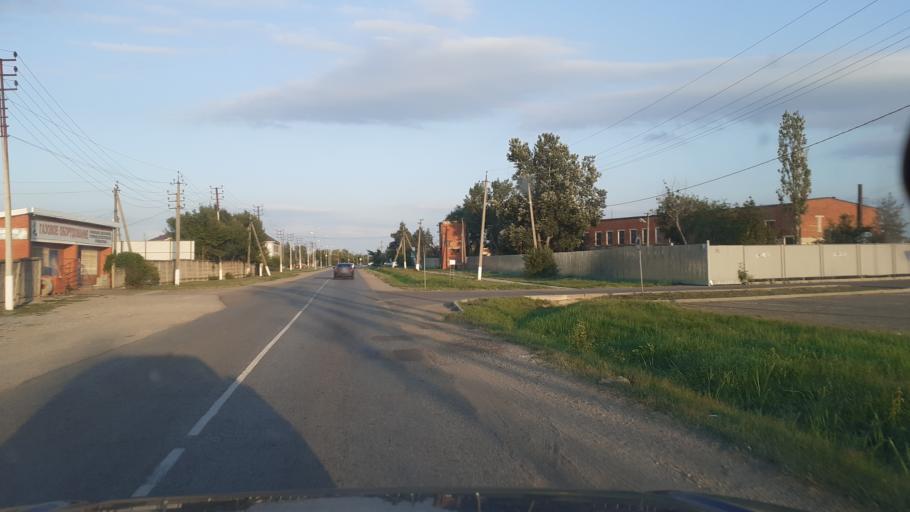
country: RU
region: Krasnodarskiy
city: Severskaya
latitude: 44.8685
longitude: 38.6646
